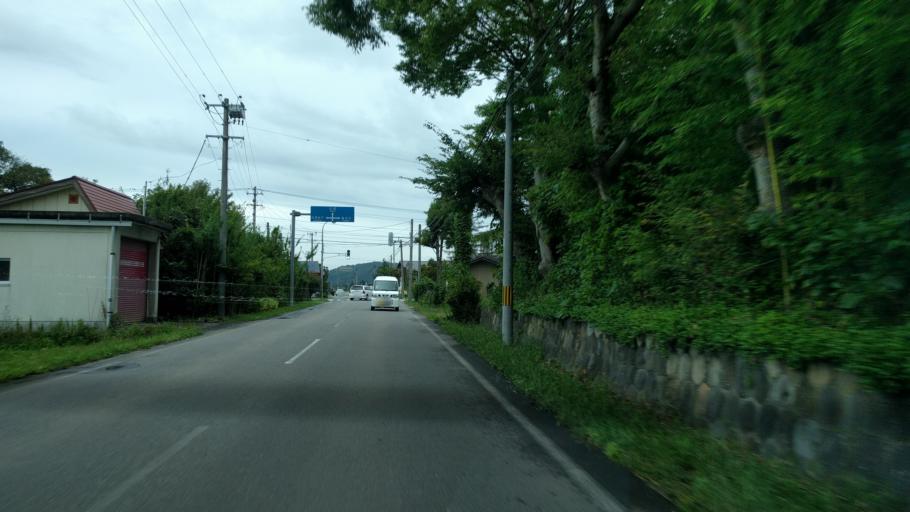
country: JP
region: Fukushima
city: Kitakata
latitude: 37.6104
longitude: 139.8572
